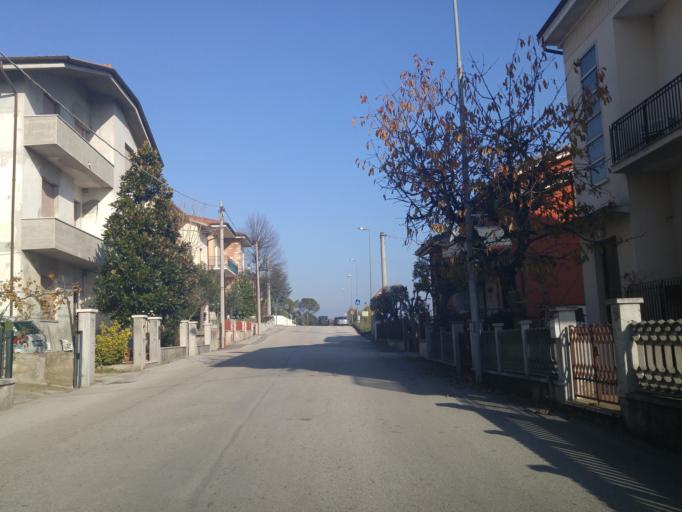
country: IT
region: The Marches
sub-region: Provincia di Pesaro e Urbino
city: Calcinelli
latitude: 43.7499
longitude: 12.9212
